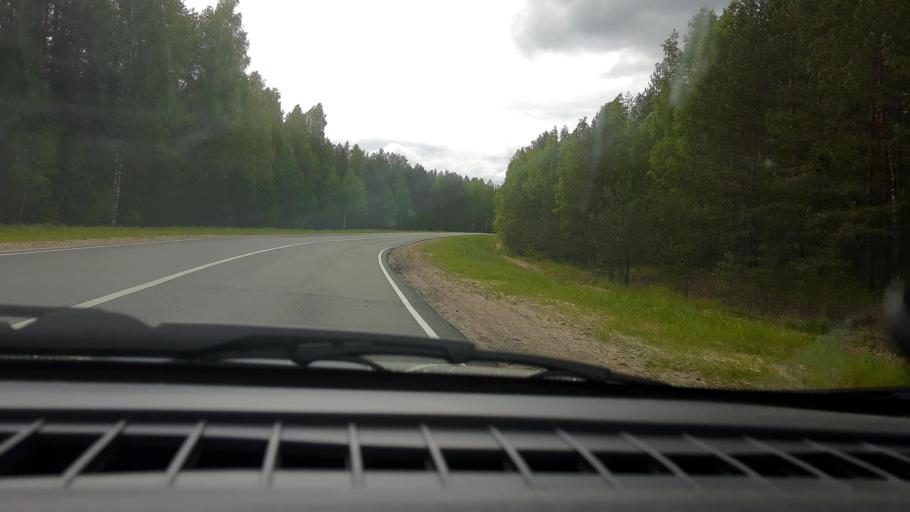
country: RU
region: Nizjnij Novgorod
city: Krasnyye Baki
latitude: 57.2038
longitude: 45.4600
